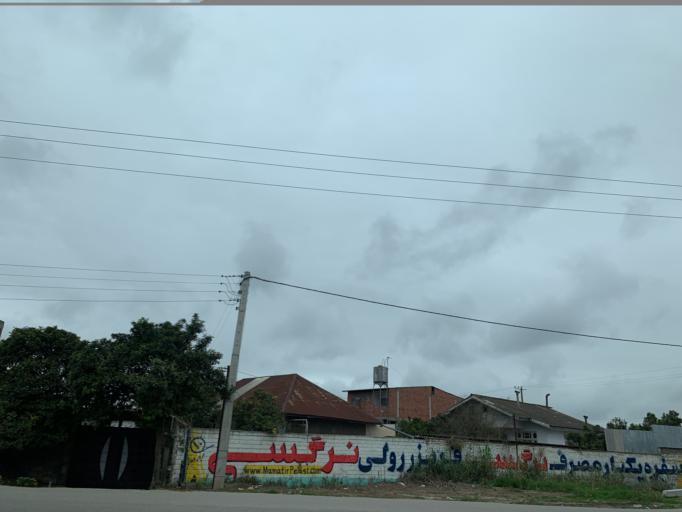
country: IR
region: Mazandaran
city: Babol
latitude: 36.5148
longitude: 52.5674
